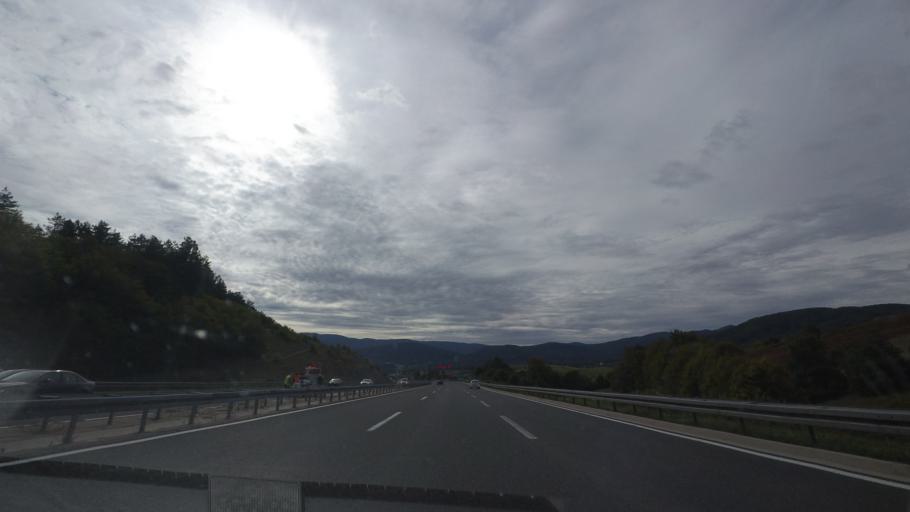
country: HR
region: Licko-Senjska
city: Brinje
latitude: 45.0140
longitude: 15.1400
